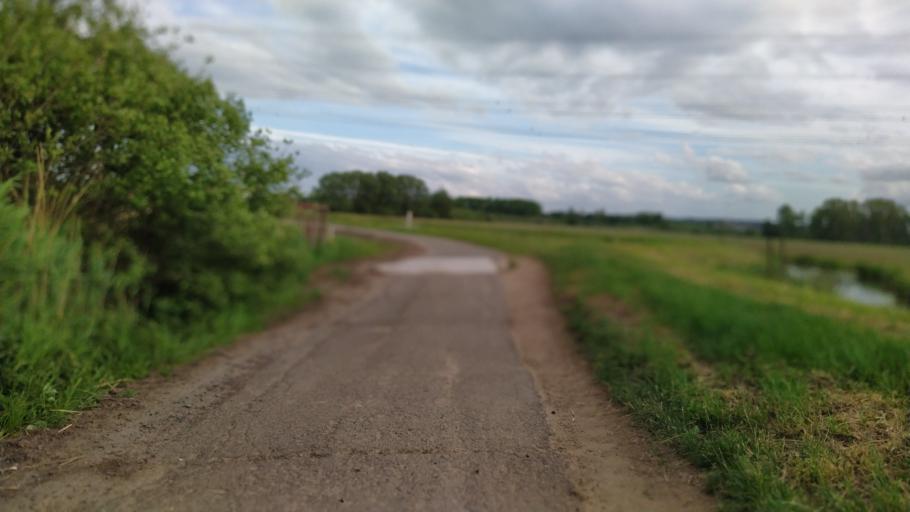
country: DE
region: Lower Saxony
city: Neu Wulmstorf
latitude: 53.4934
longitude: 9.8552
